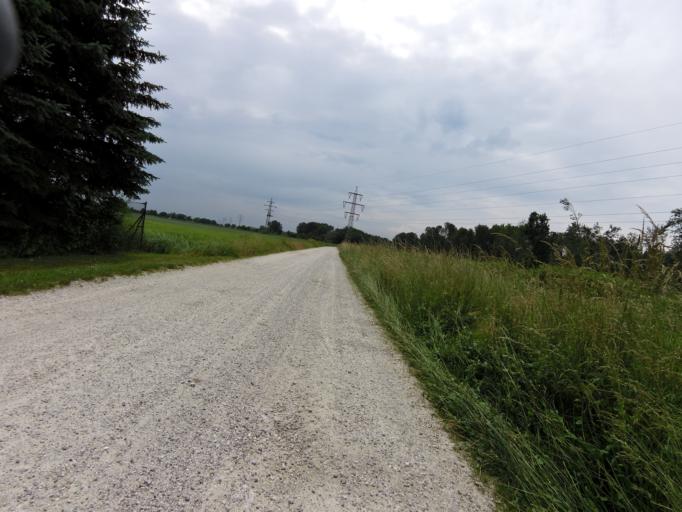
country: DE
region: Bavaria
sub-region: Upper Bavaria
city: Moosburg
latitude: 48.4759
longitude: 11.9628
